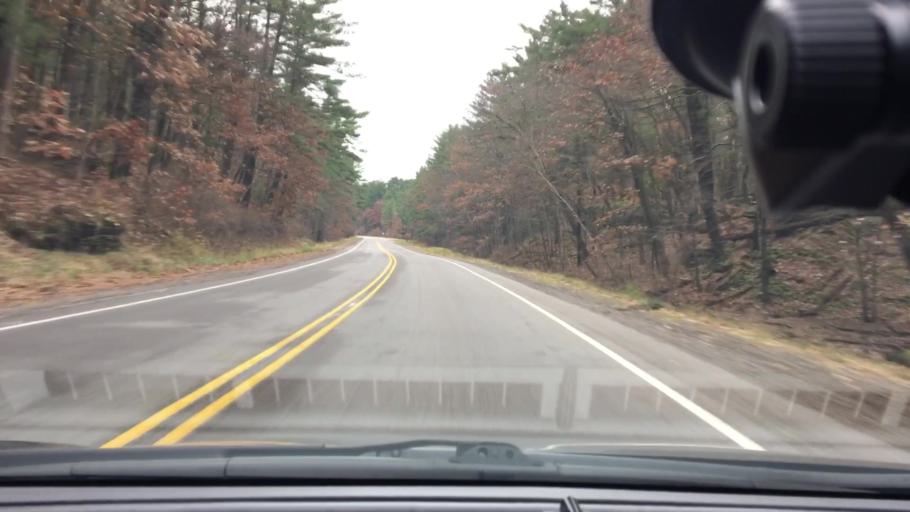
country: US
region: Wisconsin
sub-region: Columbia County
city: Wisconsin Dells
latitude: 43.6441
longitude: -89.8050
